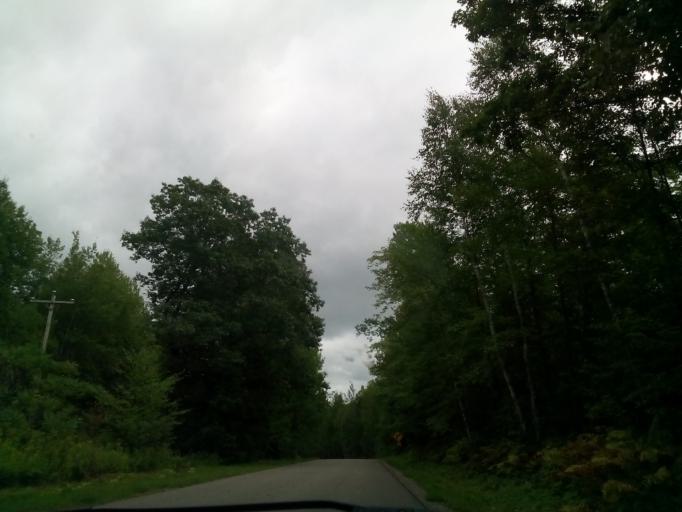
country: US
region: Wisconsin
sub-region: Menominee County
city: Legend Lake
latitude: 45.3209
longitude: -88.5250
